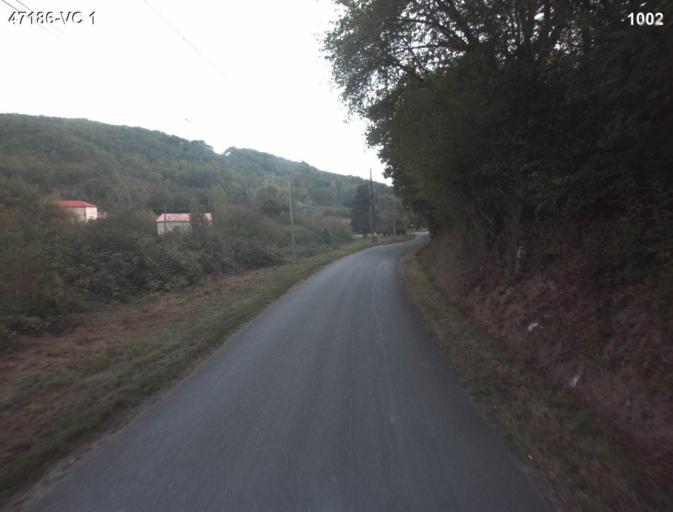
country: FR
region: Aquitaine
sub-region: Departement du Lot-et-Garonne
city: Port-Sainte-Marie
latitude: 44.1963
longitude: 0.4386
